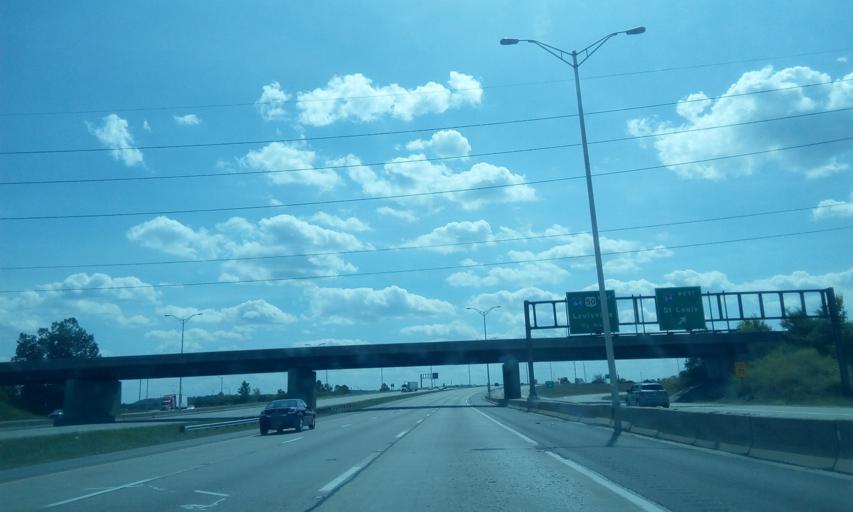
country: US
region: Illinois
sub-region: Saint Clair County
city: Washington Park
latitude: 38.6235
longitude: -90.0677
